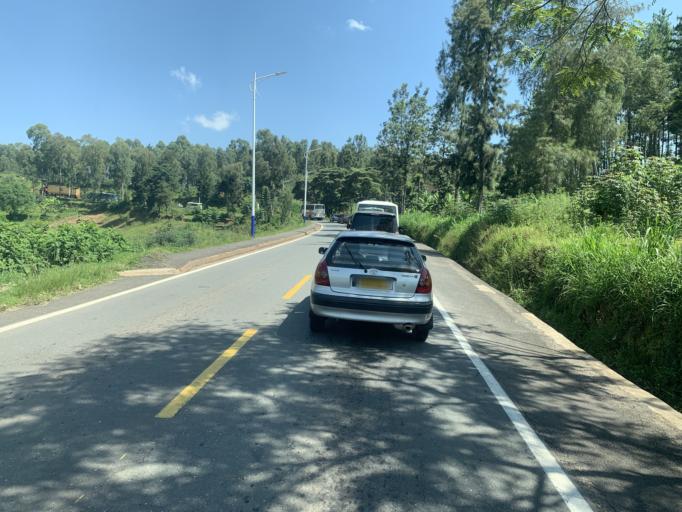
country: RW
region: Southern Province
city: Gitarama
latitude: -2.0554
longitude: 29.8029
